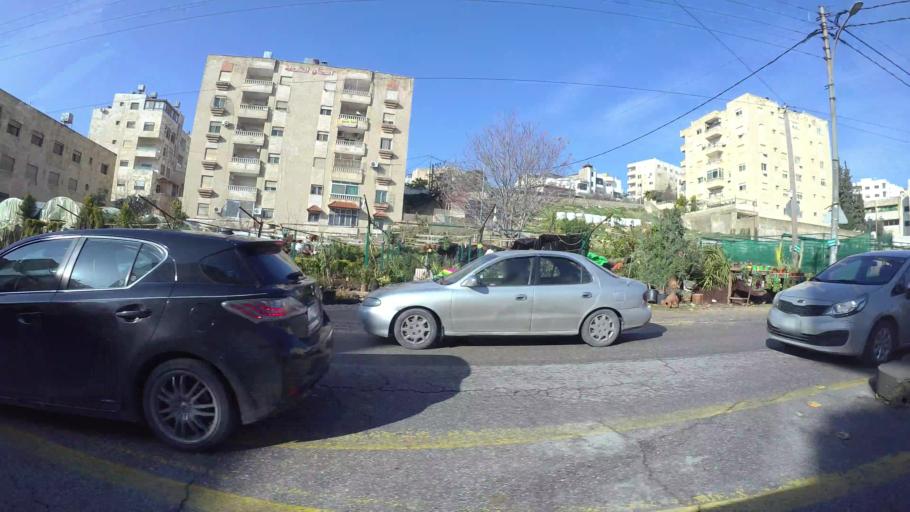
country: JO
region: Amman
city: Al Jubayhah
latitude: 31.9970
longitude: 35.8593
